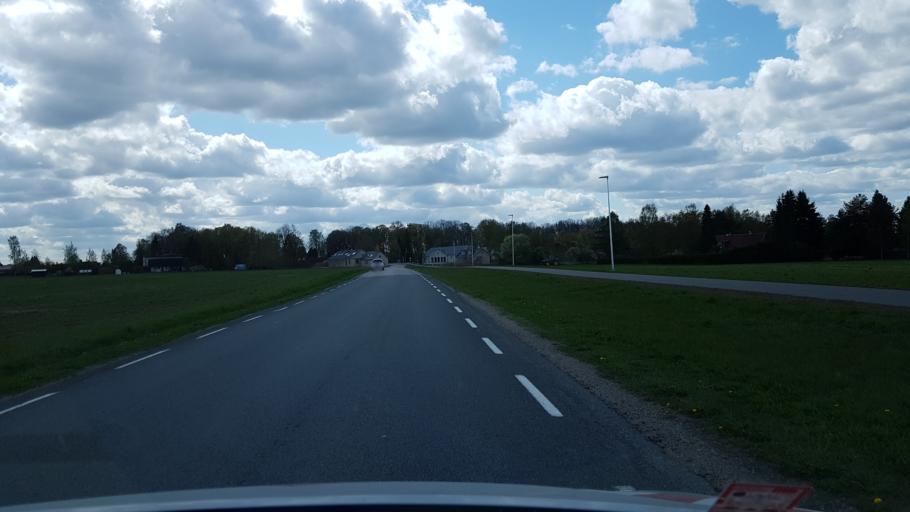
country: EE
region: Jogevamaa
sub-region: Poltsamaa linn
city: Poltsamaa
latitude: 58.7102
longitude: 25.9413
